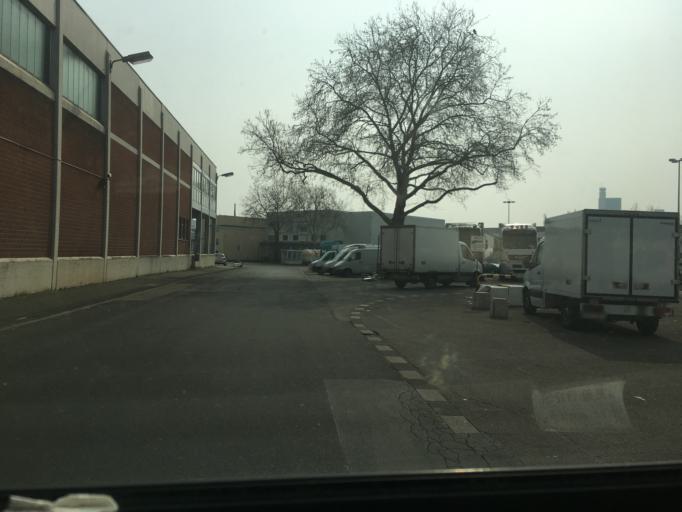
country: DE
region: North Rhine-Westphalia
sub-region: Regierungsbezirk Koln
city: Neustadt/Sued
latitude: 50.9131
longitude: 6.9542
